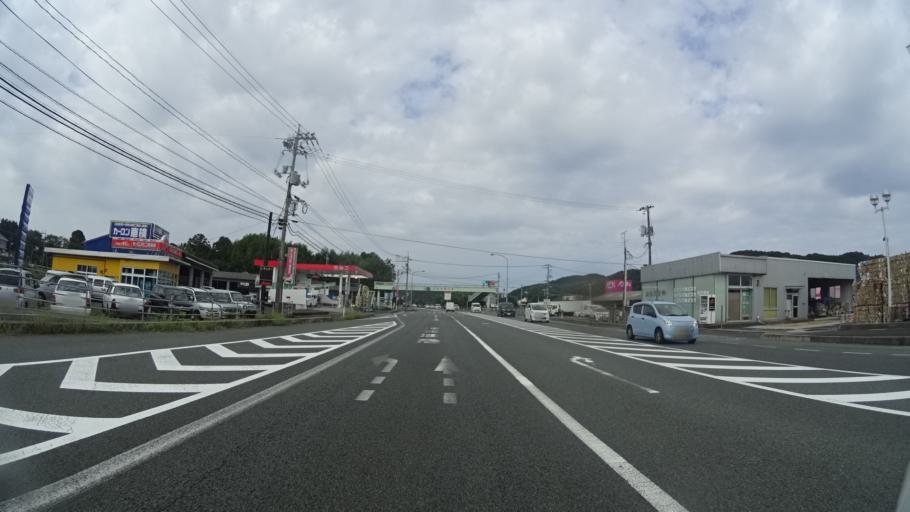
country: JP
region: Shimane
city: Odacho-oda
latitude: 35.1979
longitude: 132.4842
